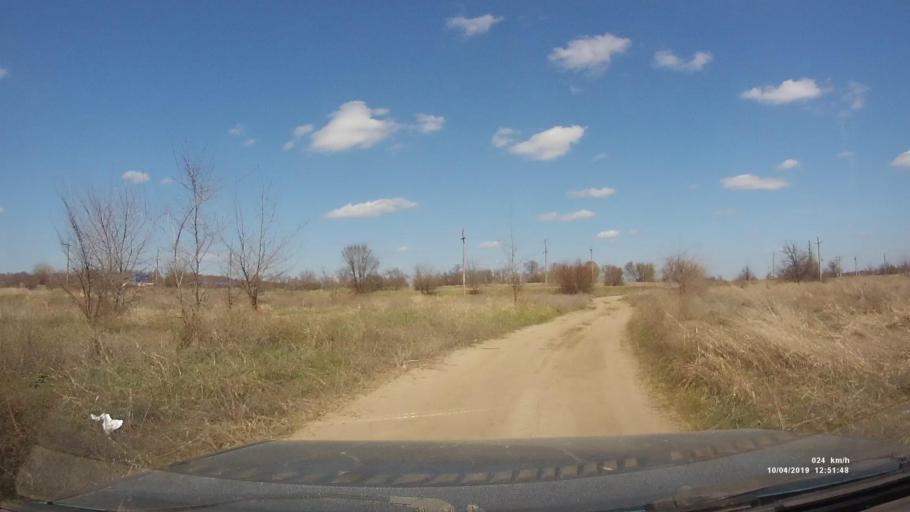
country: RU
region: Rostov
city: Kamensk-Shakhtinskiy
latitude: 48.3609
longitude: 40.2163
